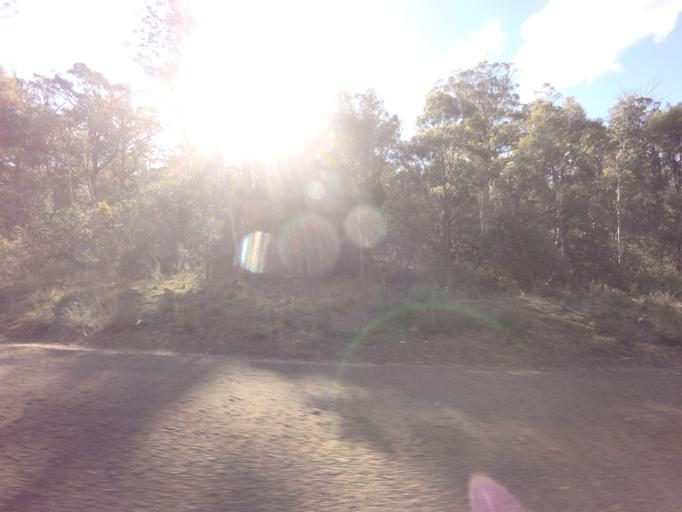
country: AU
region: Tasmania
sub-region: Break O'Day
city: St Helens
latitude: -41.8480
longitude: 148.0109
